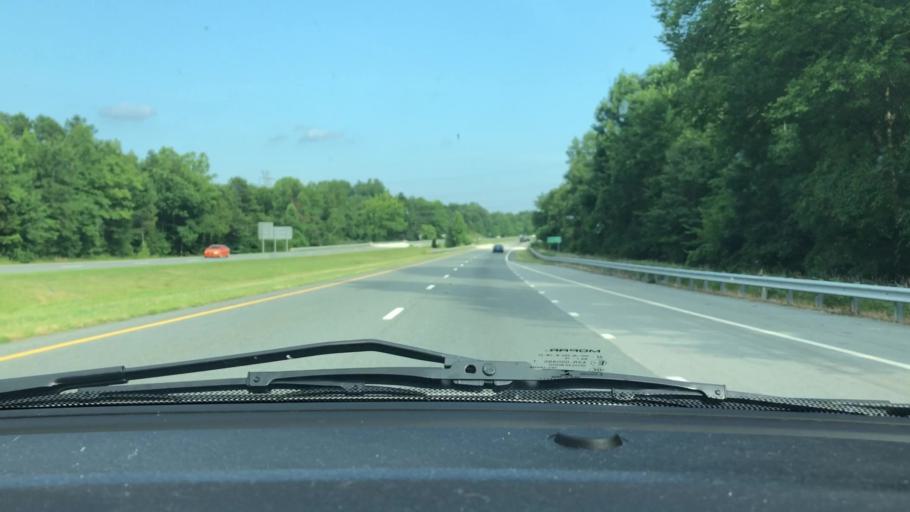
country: US
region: North Carolina
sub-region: Guilford County
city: Forest Oaks
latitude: 35.9597
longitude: -79.6982
